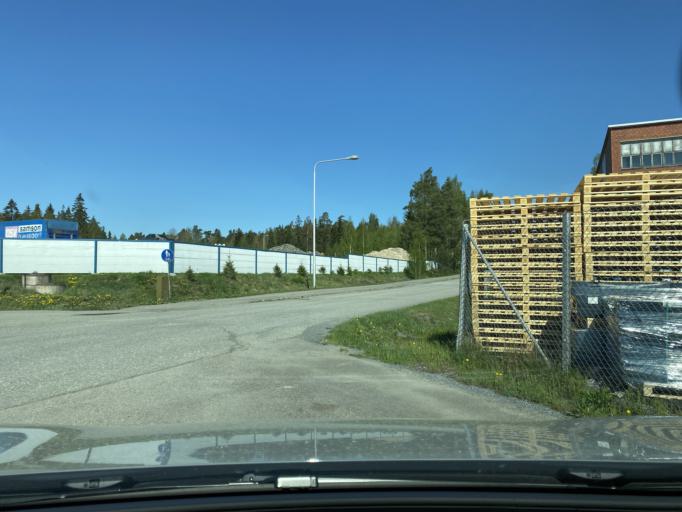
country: FI
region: Pirkanmaa
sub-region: Lounais-Pirkanmaa
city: Vammala
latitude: 61.3524
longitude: 22.8813
